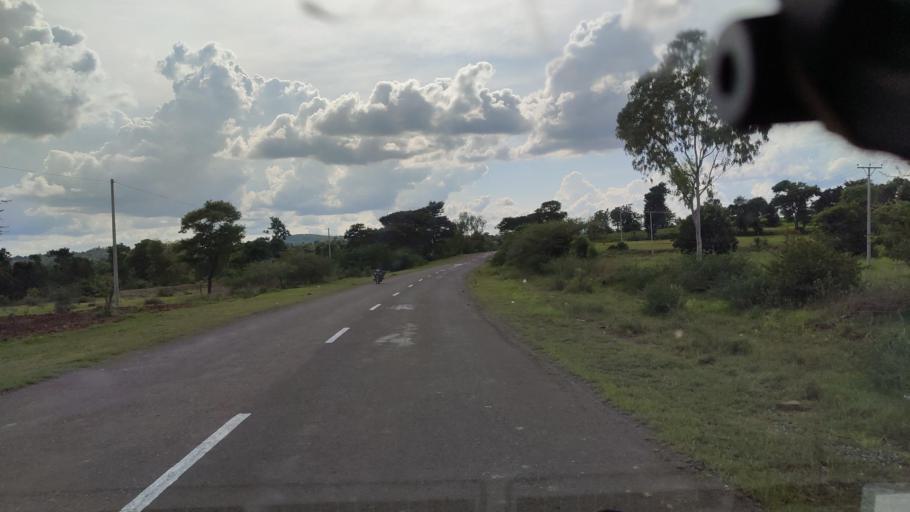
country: MM
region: Mandalay
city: Meiktila
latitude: 20.8150
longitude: 95.4508
